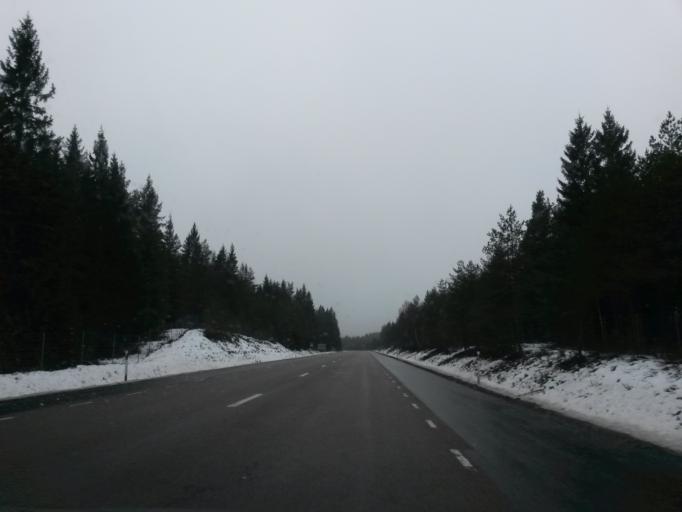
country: SE
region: Vaestra Goetaland
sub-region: Boras Kommun
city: Viskafors
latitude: 57.6270
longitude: 12.8906
